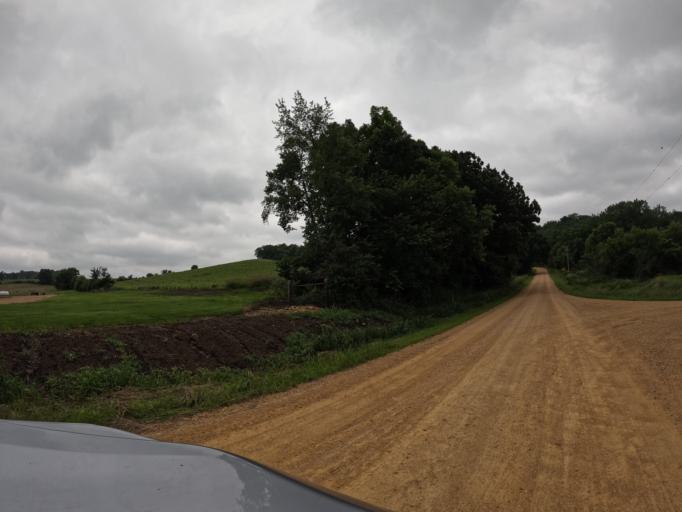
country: US
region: Illinois
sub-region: Carroll County
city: Savanna
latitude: 41.9967
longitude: -90.1797
